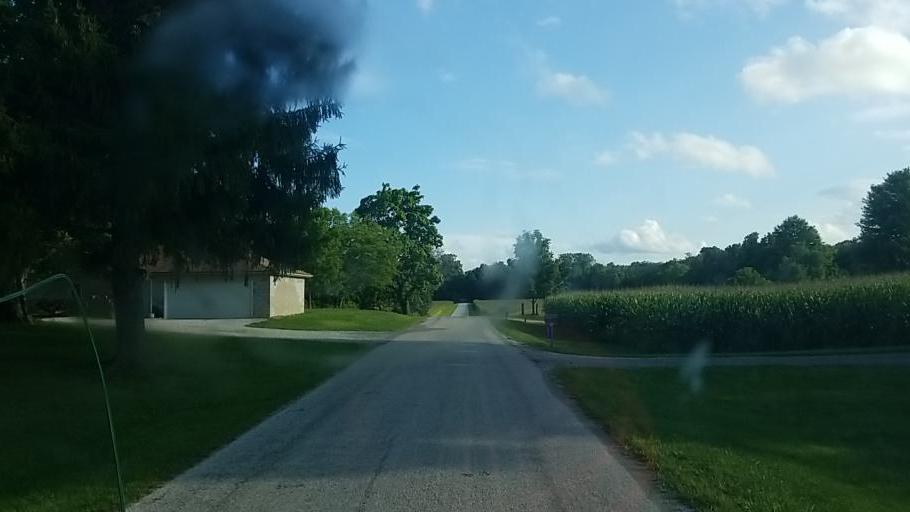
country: US
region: Ohio
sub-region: Crawford County
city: Bucyrus
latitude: 40.7748
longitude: -83.0552
